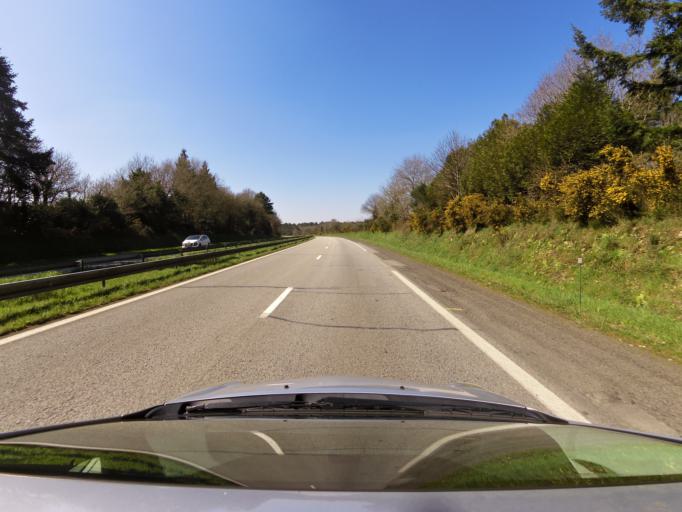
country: FR
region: Brittany
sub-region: Departement du Morbihan
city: Languidic
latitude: 47.8332
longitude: -3.1841
